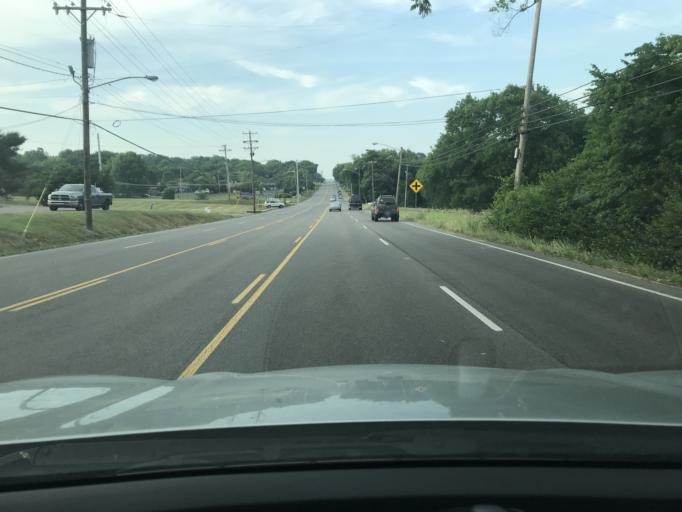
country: US
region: Tennessee
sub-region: Davidson County
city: Goodlettsville
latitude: 36.3041
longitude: -86.7194
